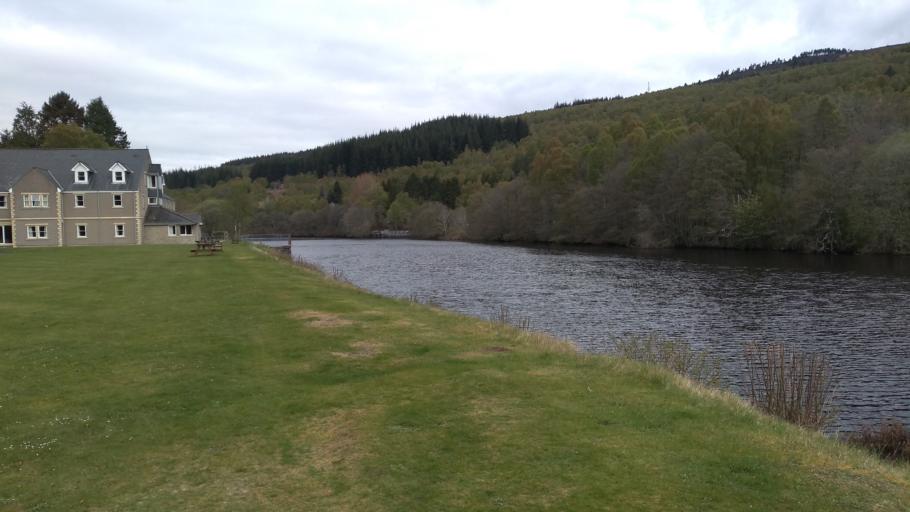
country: GB
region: Scotland
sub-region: Perth and Kinross
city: Aberfeldy
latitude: 56.7062
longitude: -4.0043
